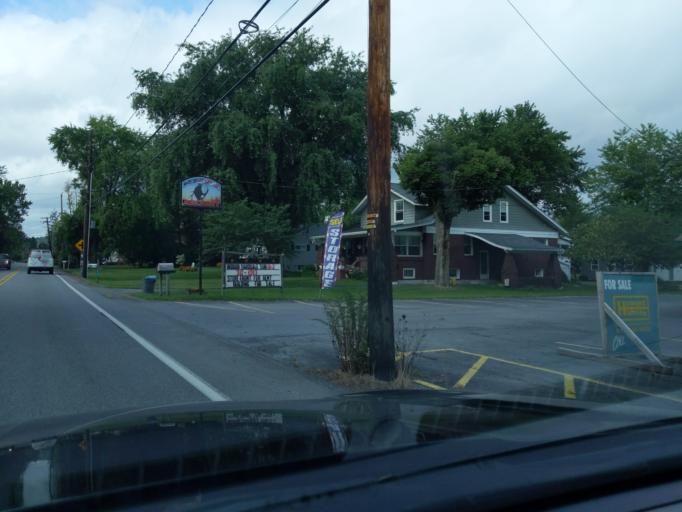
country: US
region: Pennsylvania
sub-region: Blair County
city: Roaring Spring
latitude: 40.3750
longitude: -78.4215
